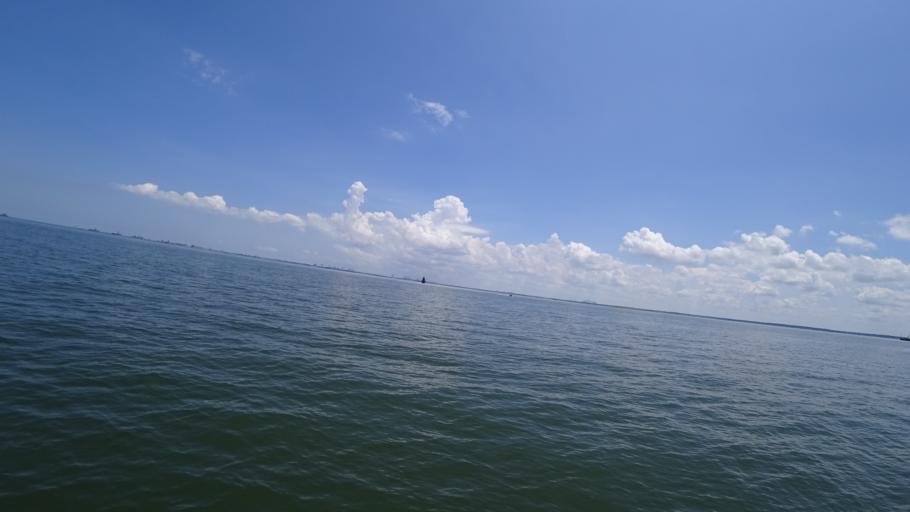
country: US
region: Virginia
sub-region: City of Newport News
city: Newport News
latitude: 36.9500
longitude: -76.3999
